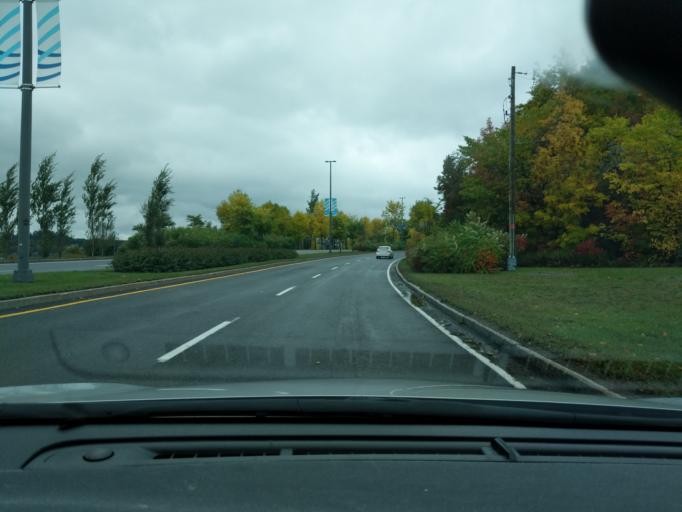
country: CA
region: Quebec
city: Quebec
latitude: 46.7600
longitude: -71.2668
